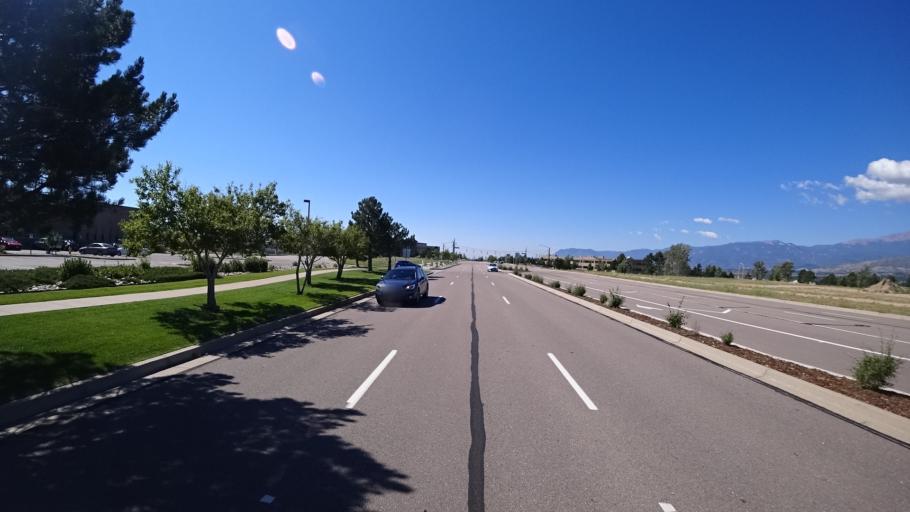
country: US
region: Colorado
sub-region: El Paso County
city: Air Force Academy
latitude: 38.9623
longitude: -104.7846
